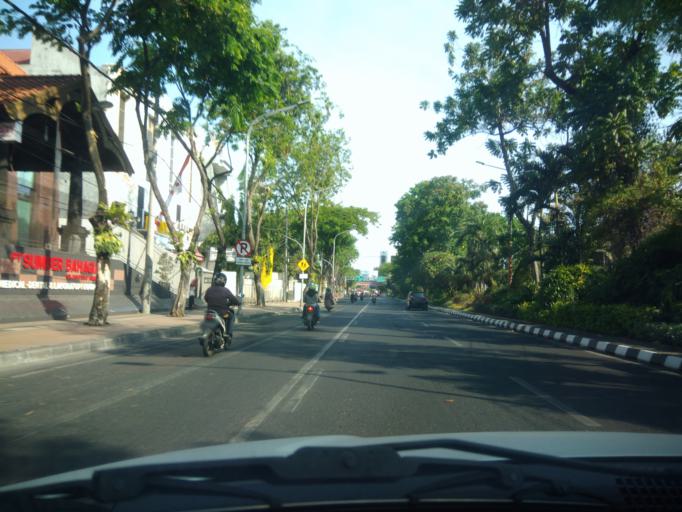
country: ID
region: East Java
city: Jagirsidosermo
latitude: -7.2936
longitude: 112.7391
